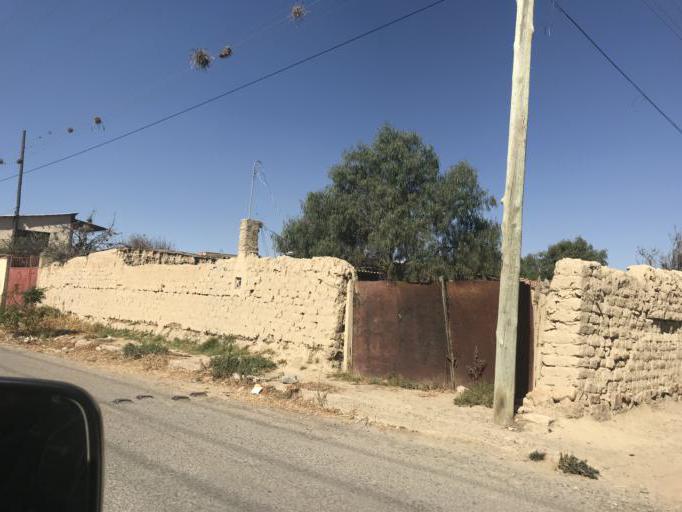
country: BO
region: Cochabamba
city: Punata
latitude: -17.5518
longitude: -65.8507
